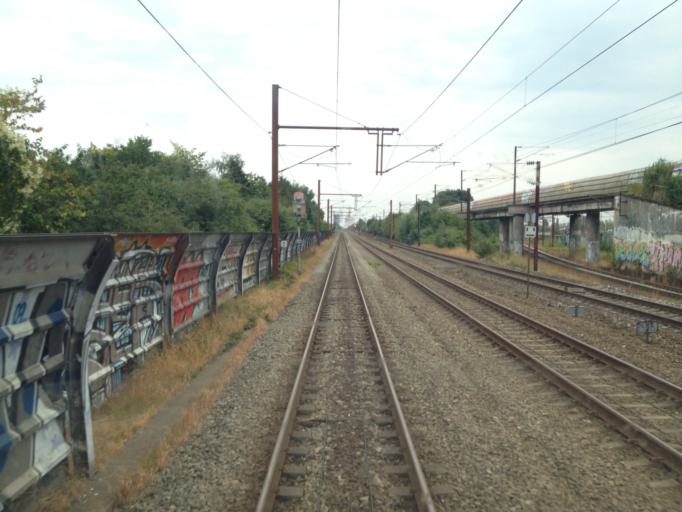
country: DK
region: Capital Region
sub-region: Hvidovre Kommune
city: Hvidovre
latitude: 55.6644
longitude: 12.4841
